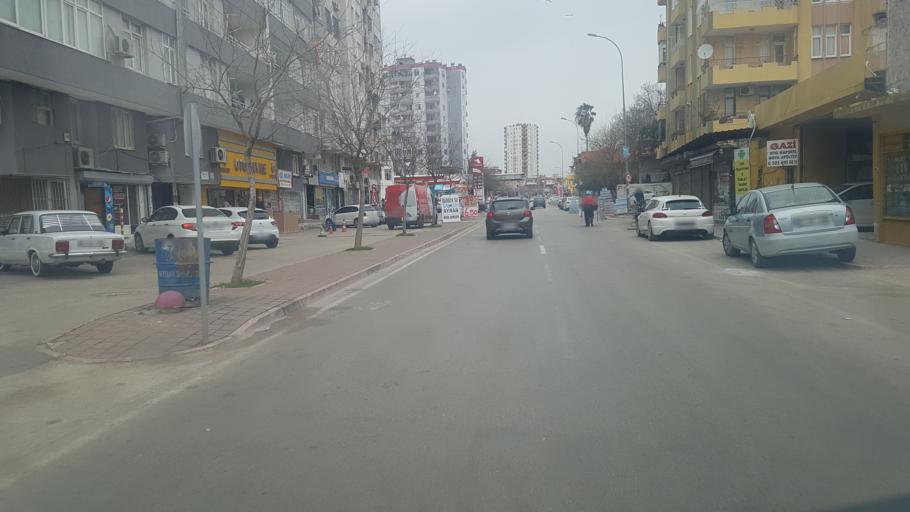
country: TR
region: Adana
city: Seyhan
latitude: 37.0071
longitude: 35.3092
